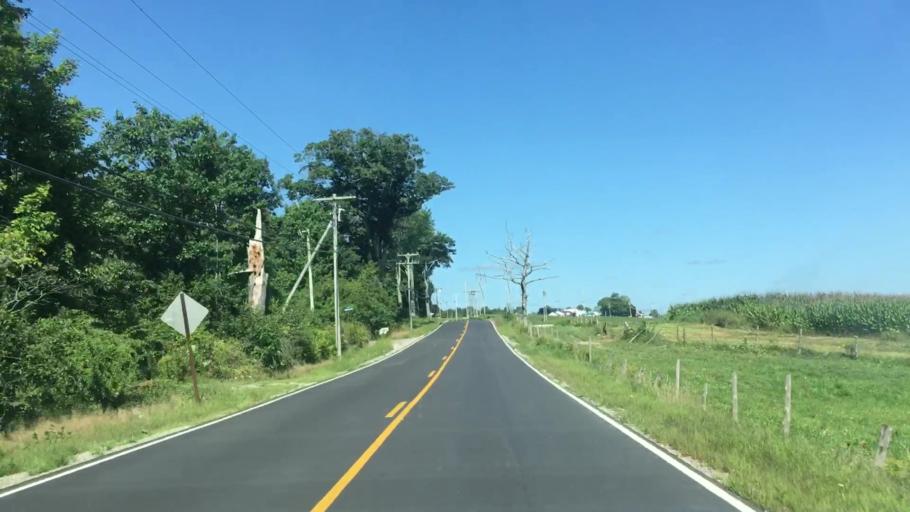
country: US
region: Maine
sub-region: Sagadahoc County
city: Topsham
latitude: 43.9563
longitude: -69.9739
